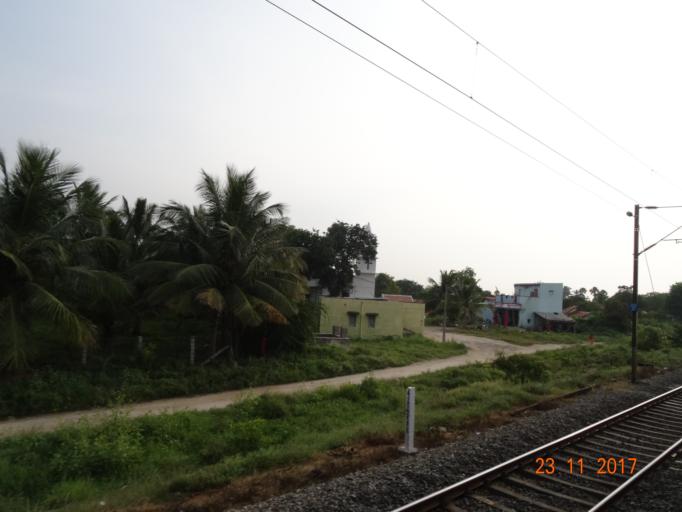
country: IN
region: Tamil Nadu
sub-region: Tiruppur
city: Uttukkuli
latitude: 11.1860
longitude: 77.4926
